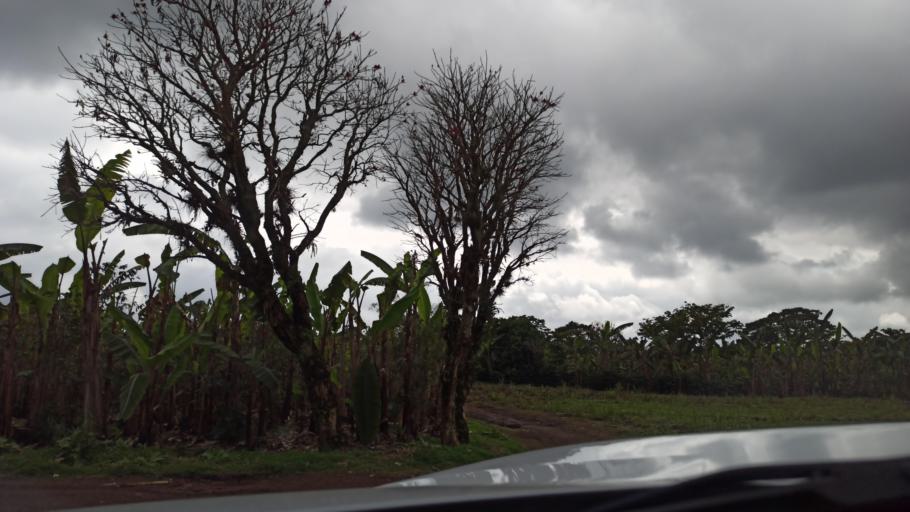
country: MX
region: Veracruz
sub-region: Fortin
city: Santa Lucia Potrerillo
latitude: 18.9666
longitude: -97.0289
